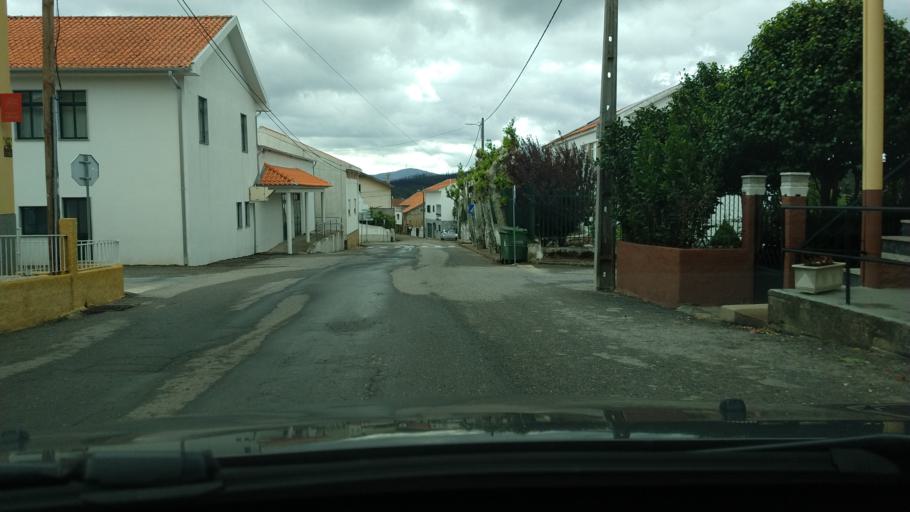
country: PT
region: Castelo Branco
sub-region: Covilha
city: Covilha
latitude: 40.2261
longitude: -7.6485
